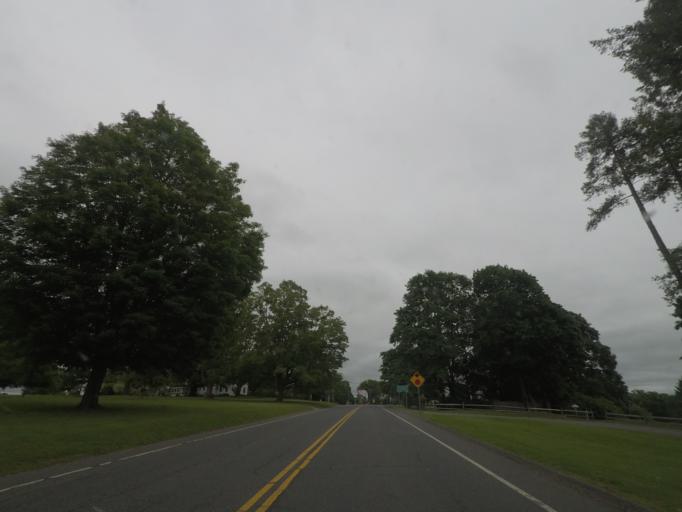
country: US
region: Connecticut
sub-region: Litchfield County
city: Canaan
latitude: 41.9427
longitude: -73.4408
